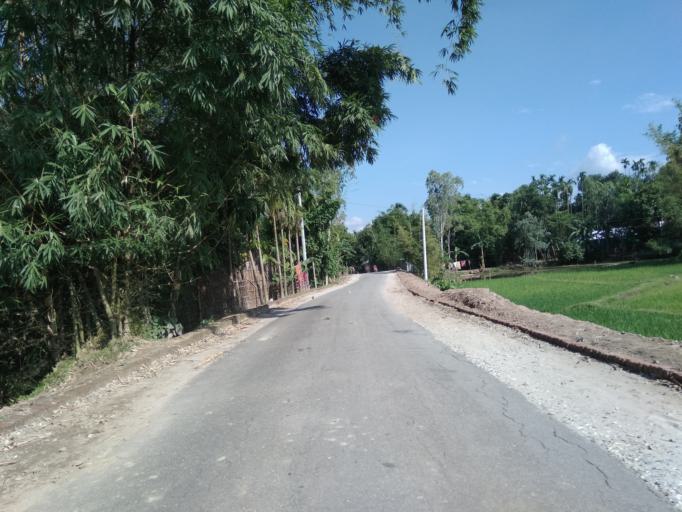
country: BD
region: Rangpur Division
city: Panchagarh
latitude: 26.2562
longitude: 88.6151
